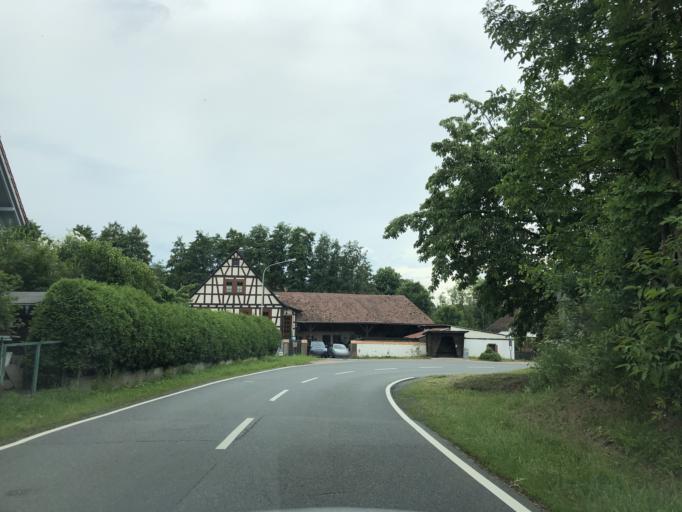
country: DE
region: Hesse
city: Lutzelbach
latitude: 49.7368
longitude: 8.7454
